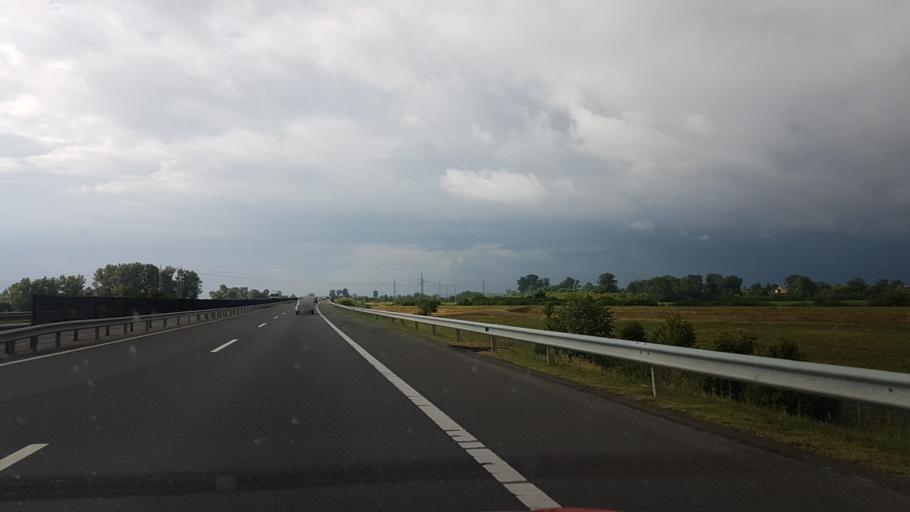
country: HU
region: Borsod-Abauj-Zemplen
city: Felsozsolca
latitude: 48.0925
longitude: 20.8495
